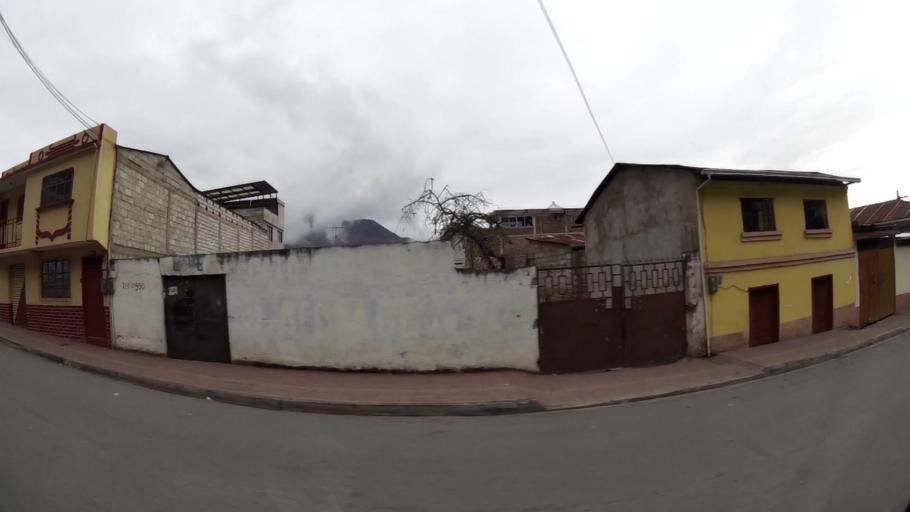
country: EC
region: Chimborazo
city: Alausi
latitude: -2.2892
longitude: -78.9179
